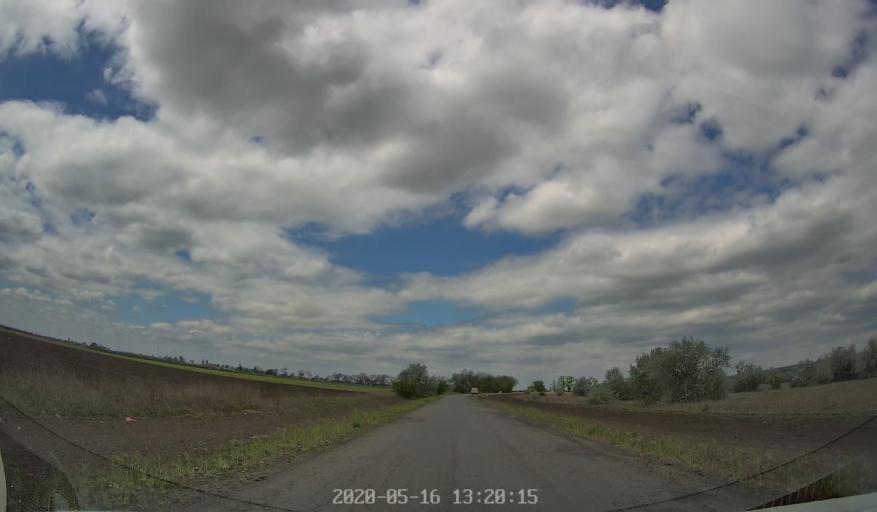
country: UA
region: Odessa
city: Lymanske
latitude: 46.5389
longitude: 30.0503
